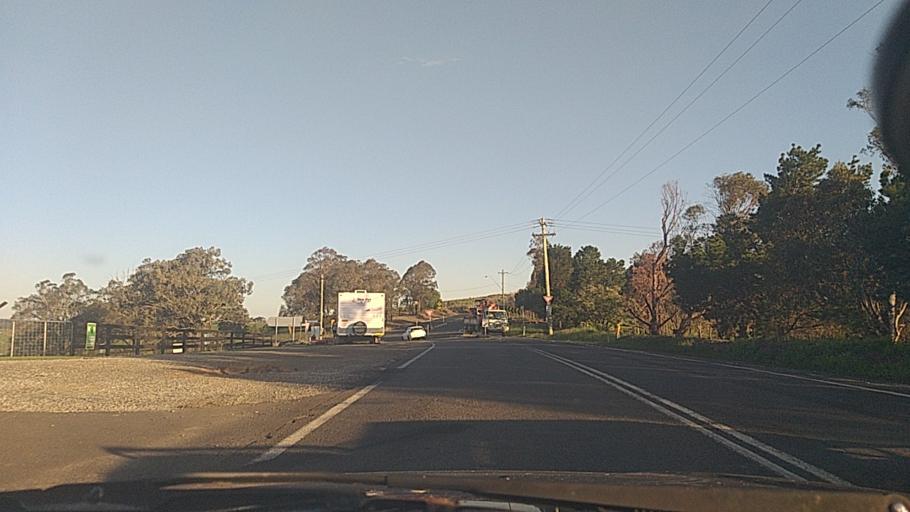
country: AU
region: New South Wales
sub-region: Wollondilly
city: Douglas Park
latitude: -34.1478
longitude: 150.7210
